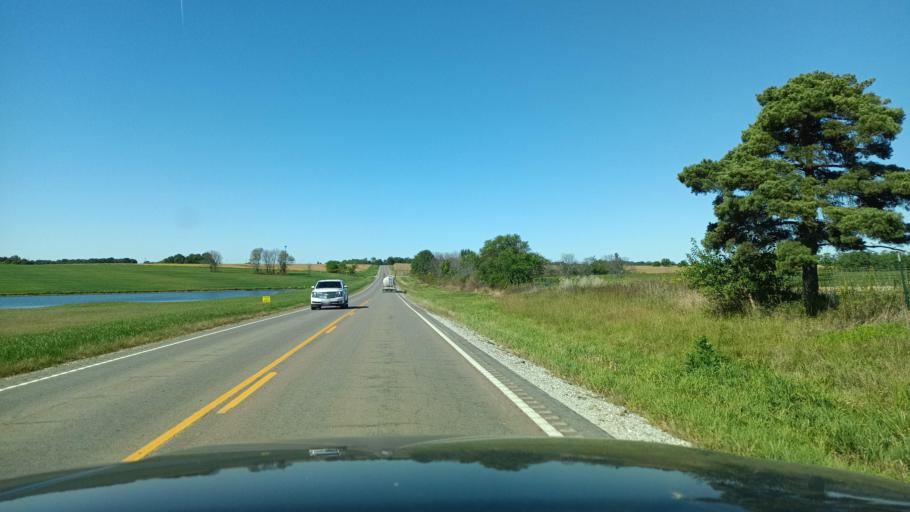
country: US
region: Missouri
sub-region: Scotland County
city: Memphis
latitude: 40.4556
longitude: -92.0724
